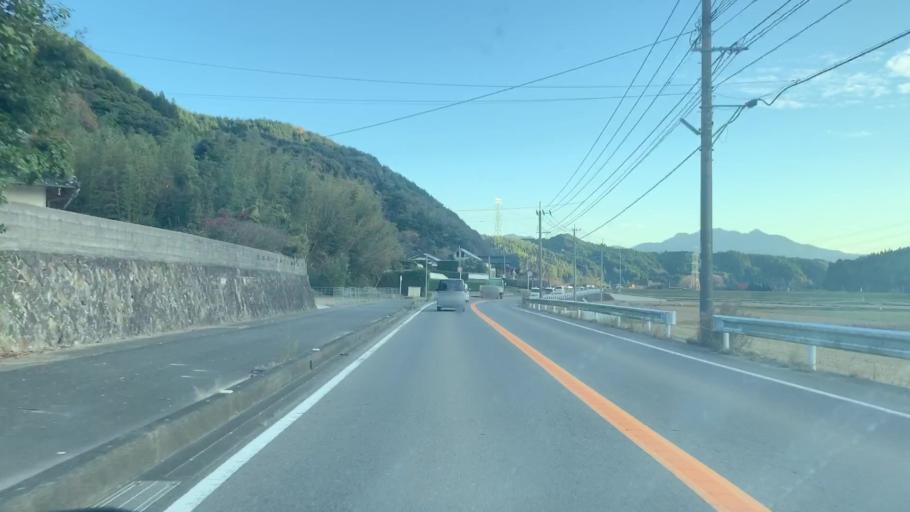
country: JP
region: Saga Prefecture
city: Karatsu
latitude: 33.3685
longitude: 130.0046
